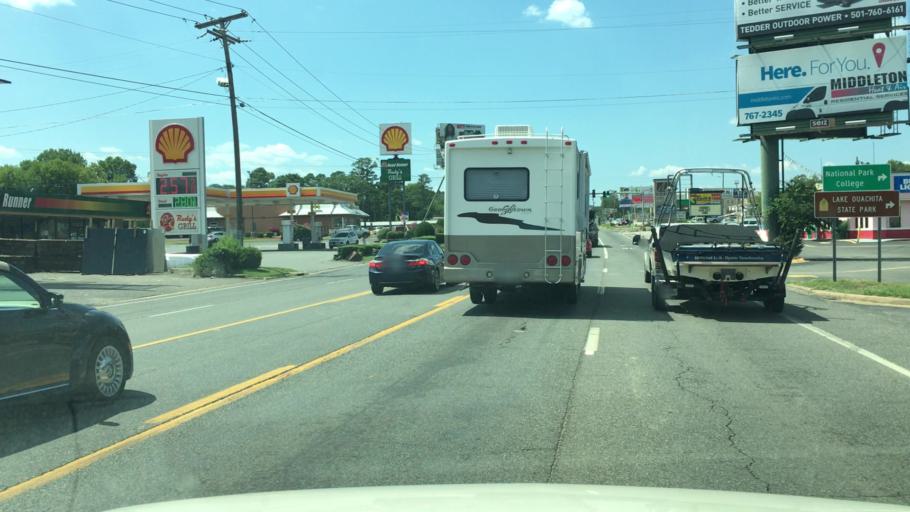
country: US
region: Arkansas
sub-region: Garland County
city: Piney
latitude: 34.5024
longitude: -93.1247
